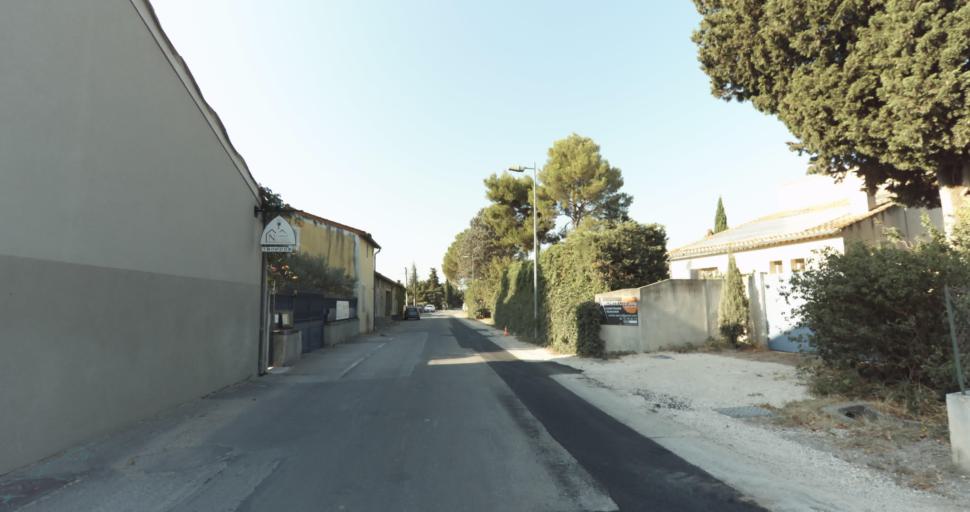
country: FR
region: Provence-Alpes-Cote d'Azur
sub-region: Departement du Vaucluse
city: Monteux
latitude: 44.0301
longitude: 4.9967
